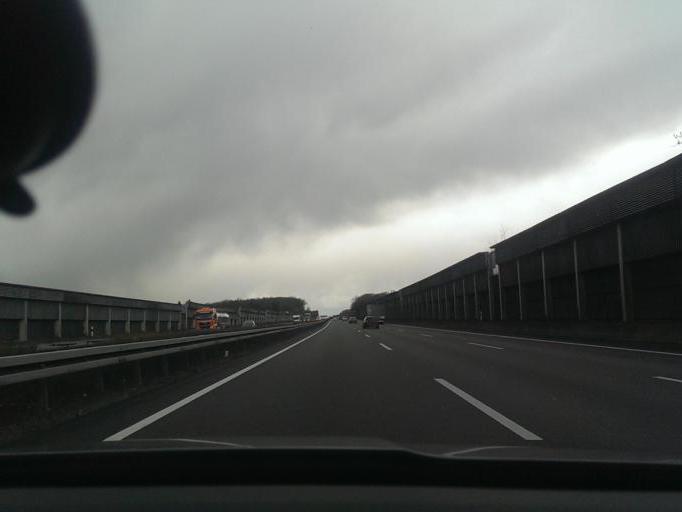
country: DE
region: Lower Saxony
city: Lehre
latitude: 52.3107
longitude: 10.5984
